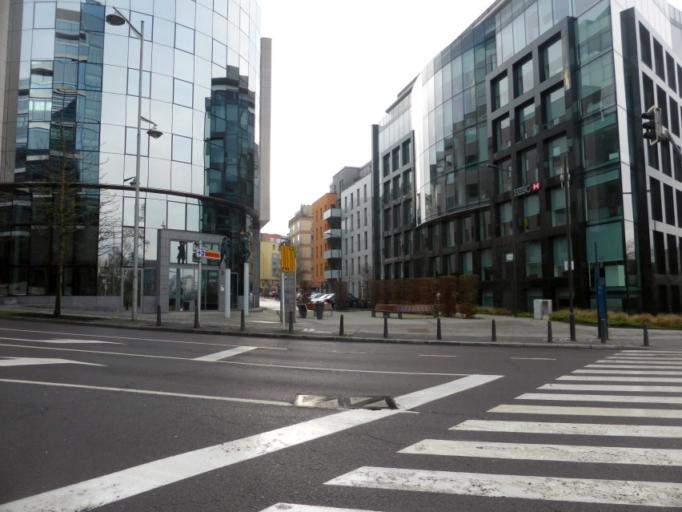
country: LU
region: Luxembourg
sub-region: Canton de Luxembourg
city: Luxembourg
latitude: 49.6048
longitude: 6.1374
